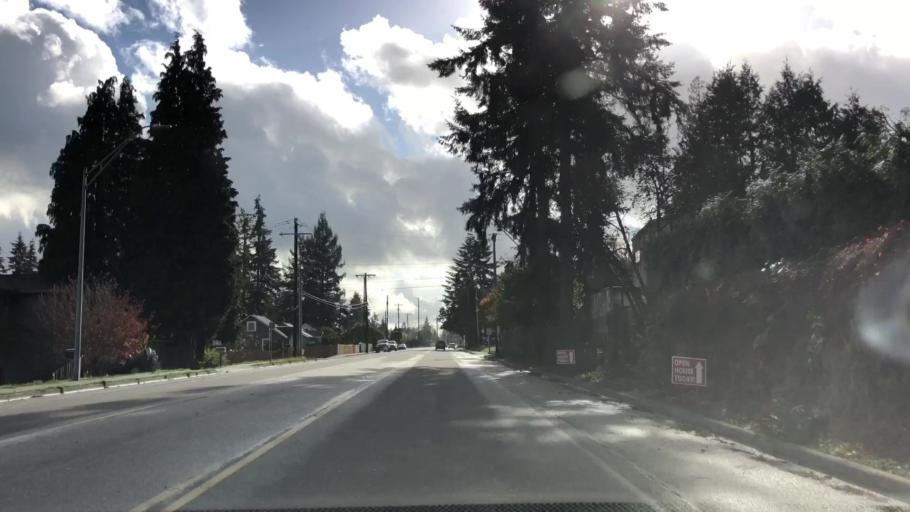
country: US
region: Washington
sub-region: Snohomish County
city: Everett
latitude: 47.9441
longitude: -122.2068
